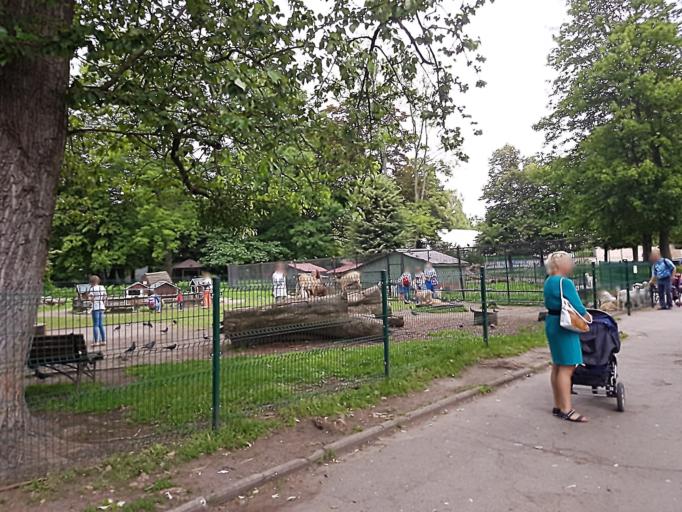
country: RU
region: Kaliningrad
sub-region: Gorod Kaliningrad
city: Kaliningrad
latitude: 54.7236
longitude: 20.4893
